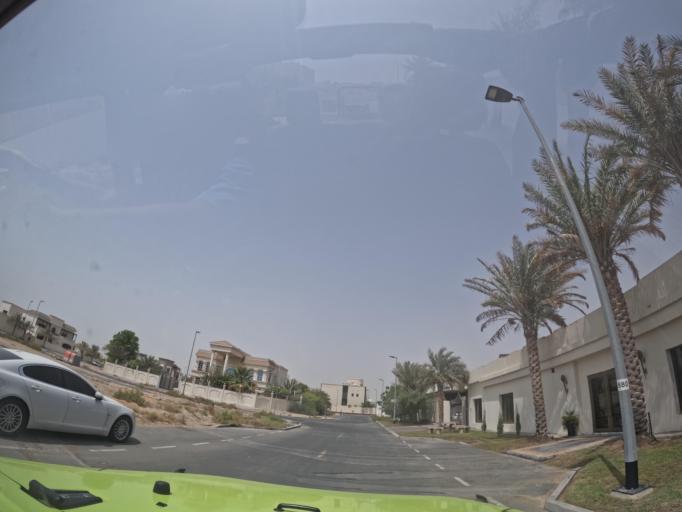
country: AE
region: Dubai
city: Dubai
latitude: 25.1336
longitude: 55.3616
